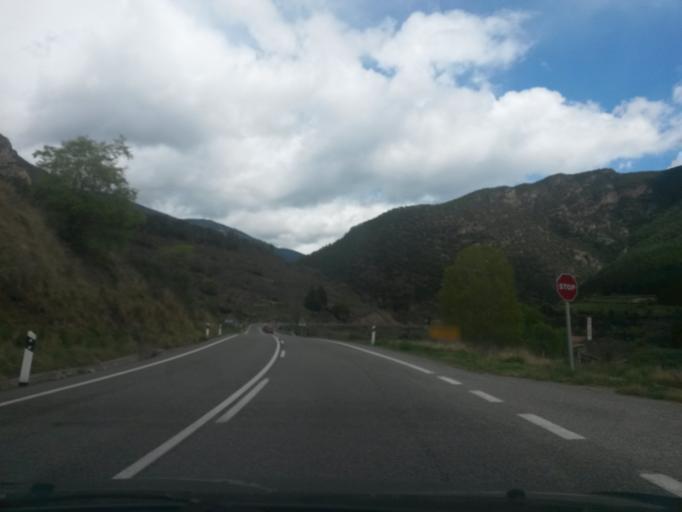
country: ES
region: Catalonia
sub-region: Provincia de Lleida
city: el Pont de Bar
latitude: 42.3592
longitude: 1.5802
